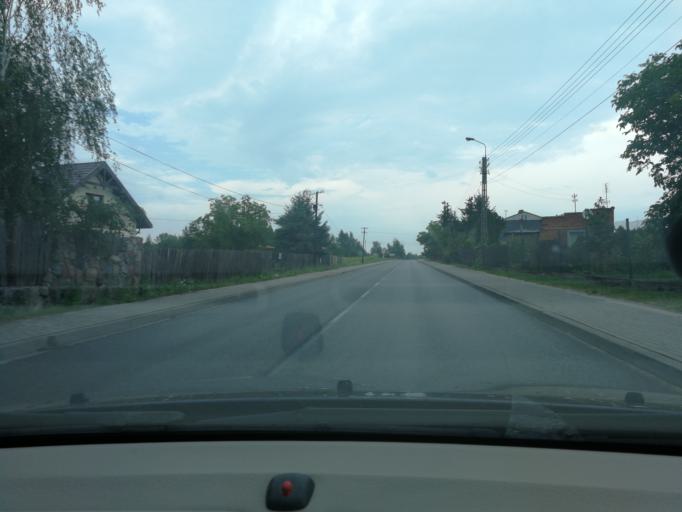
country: PL
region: Masovian Voivodeship
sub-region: Powiat zyrardowski
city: Radziejowice
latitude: 52.0058
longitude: 20.5564
